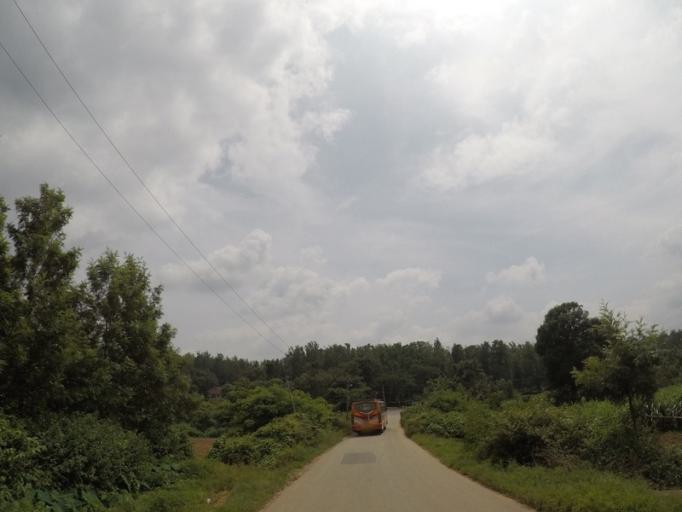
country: IN
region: Karnataka
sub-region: Chikmagalur
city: Chikmagalur
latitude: 13.4404
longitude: 75.8049
